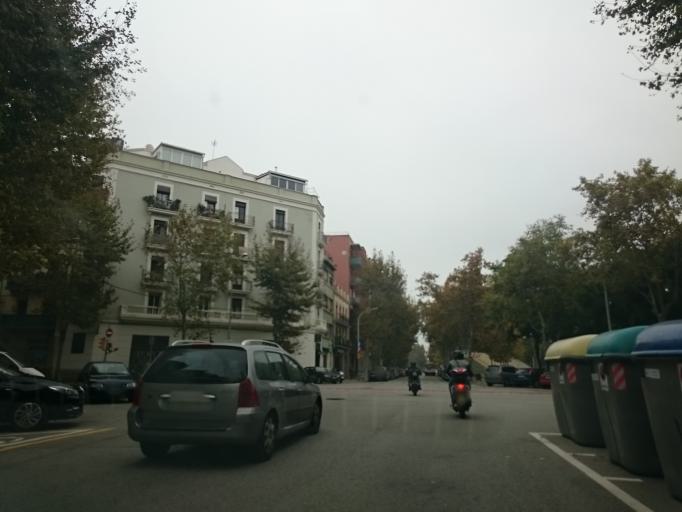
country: ES
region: Catalonia
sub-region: Provincia de Barcelona
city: Sant Marti
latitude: 41.4051
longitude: 2.2048
